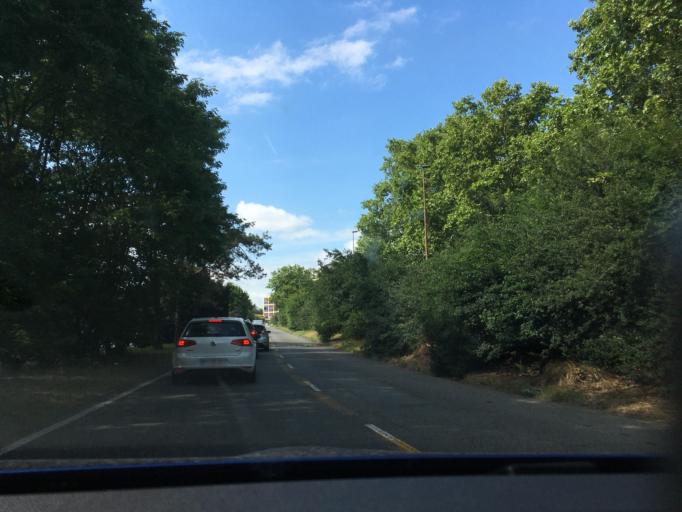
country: FR
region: Midi-Pyrenees
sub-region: Departement de la Haute-Garonne
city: Portet-sur-Garonne
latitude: 43.5752
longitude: 1.3959
